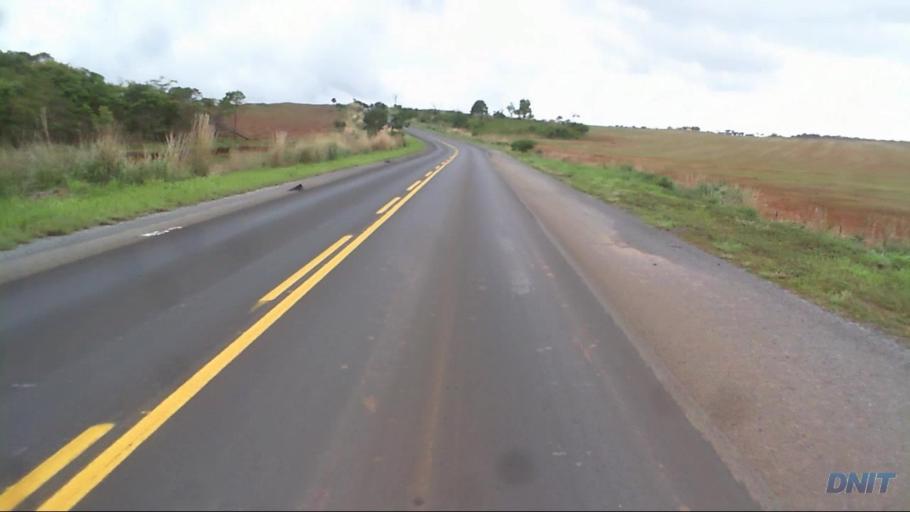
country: BR
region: Goias
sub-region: Padre Bernardo
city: Padre Bernardo
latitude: -15.2154
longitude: -48.5036
